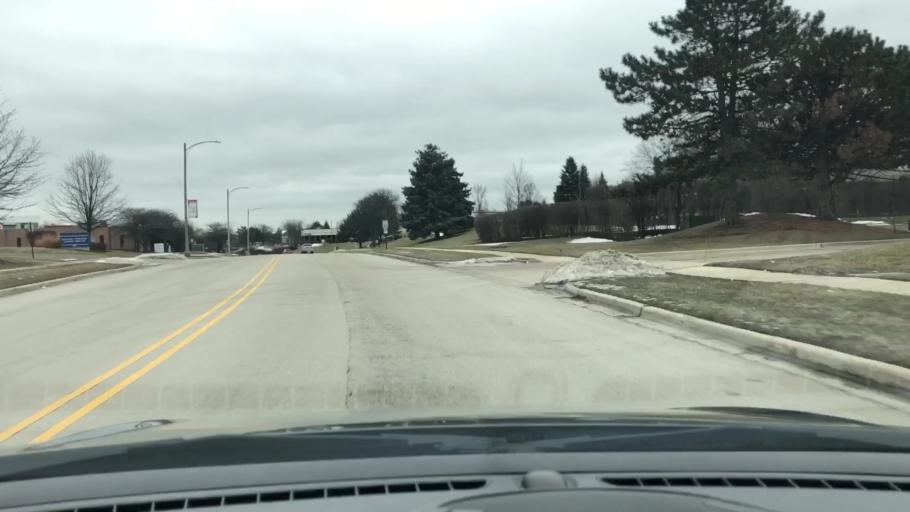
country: US
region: Illinois
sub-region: DuPage County
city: Clarendon Hills
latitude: 41.8158
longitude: -87.9546
